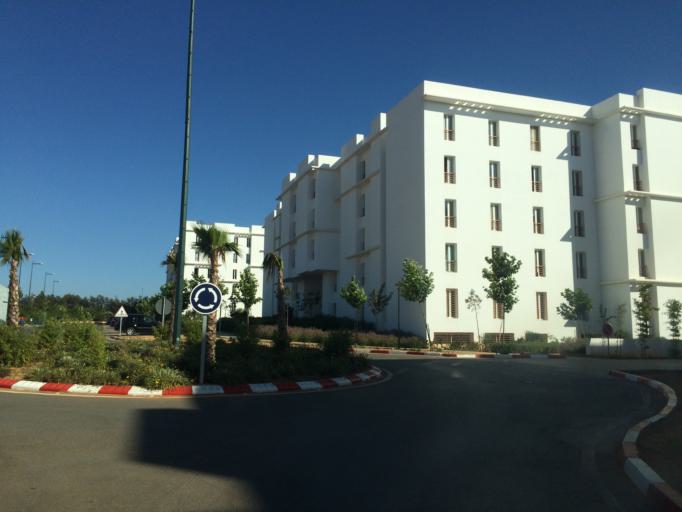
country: MA
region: Rabat-Sale-Zemmour-Zaer
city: Sale
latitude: 33.9869
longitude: -6.7219
